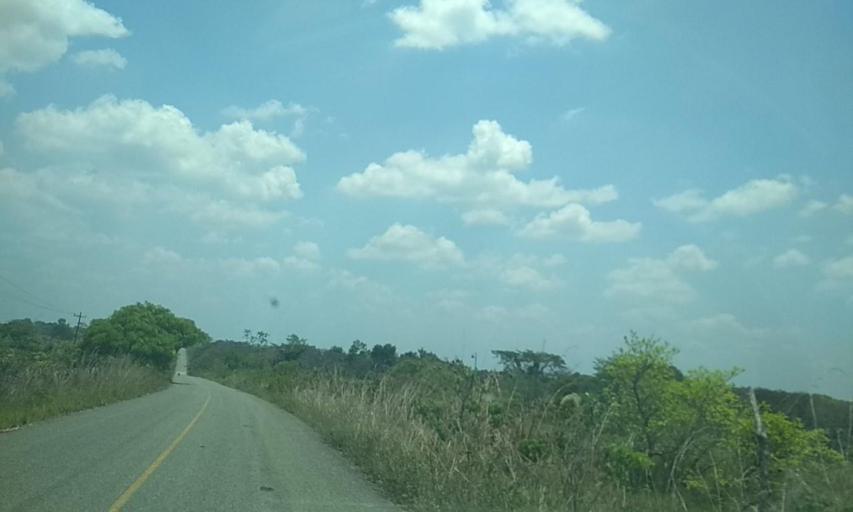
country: MX
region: Tabasco
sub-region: Huimanguillo
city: Francisco Rueda
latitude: 17.8228
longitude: -93.8717
